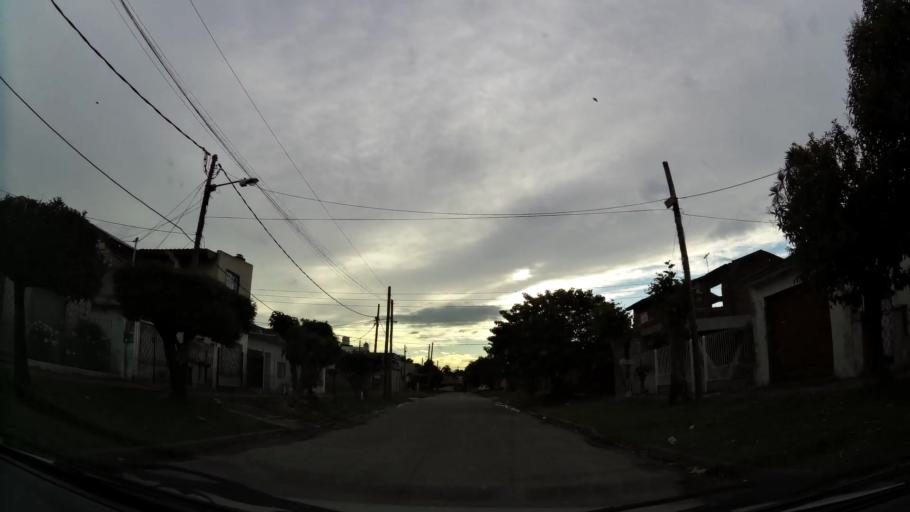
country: AR
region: Buenos Aires
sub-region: Partido de Lomas de Zamora
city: Lomas de Zamora
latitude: -34.7464
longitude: -58.3459
